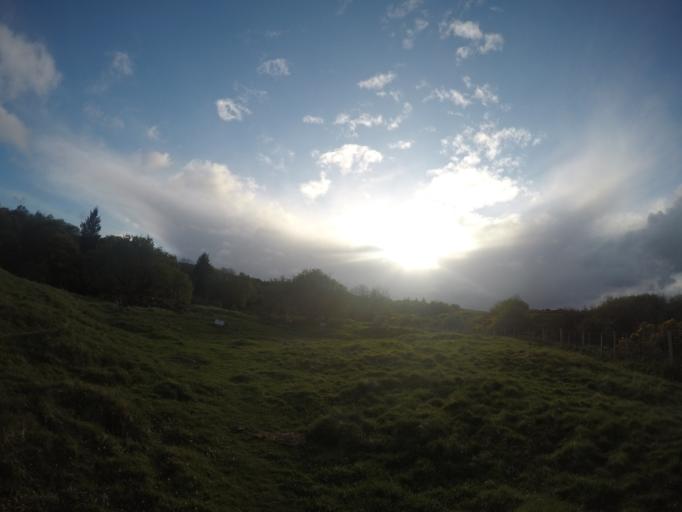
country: GB
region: Scotland
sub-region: Highland
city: Isle of Skye
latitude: 57.4533
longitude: -6.3056
